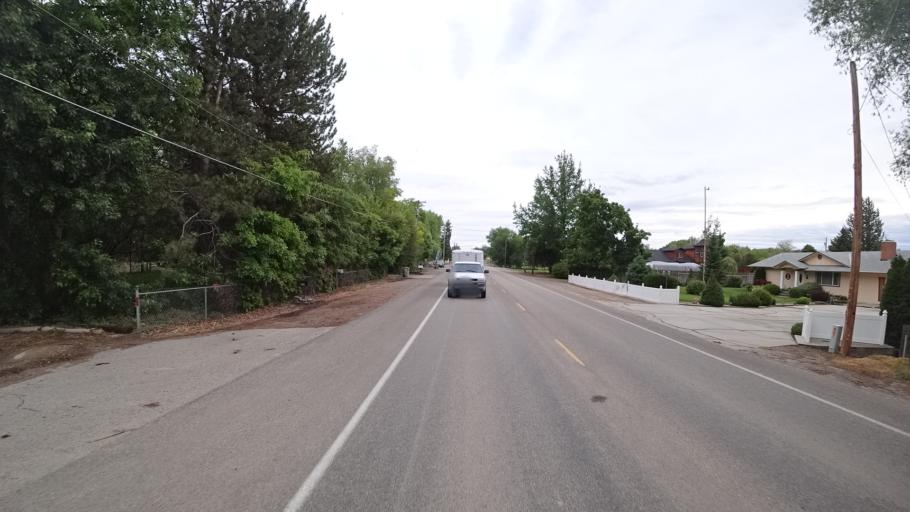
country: US
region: Idaho
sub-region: Ada County
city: Star
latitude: 43.6879
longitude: -116.4933
